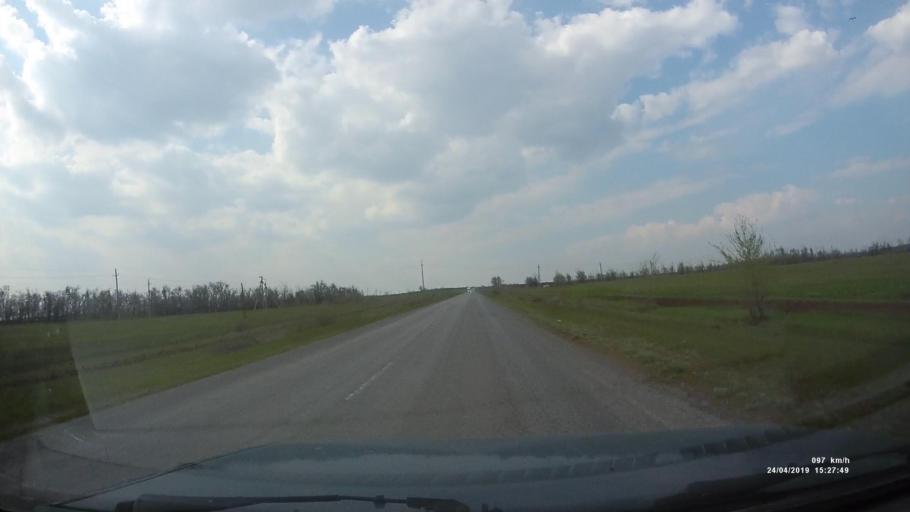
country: RU
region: Rostov
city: Remontnoye
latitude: 46.5688
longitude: 43.0237
